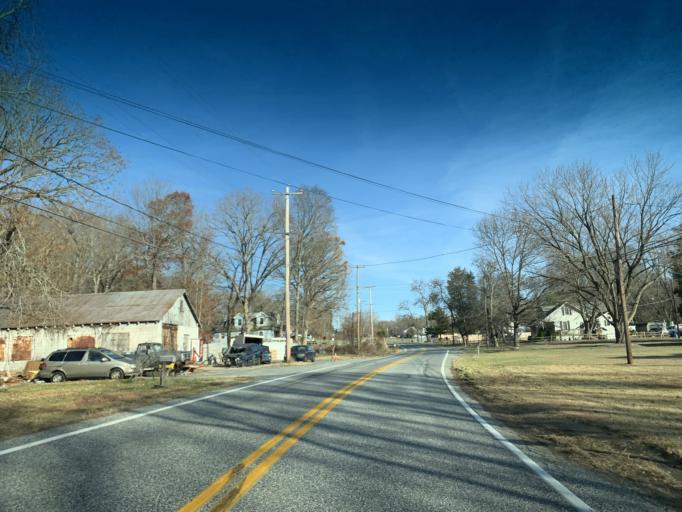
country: US
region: Maryland
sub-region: Cecil County
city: North East
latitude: 39.5974
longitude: -75.9632
